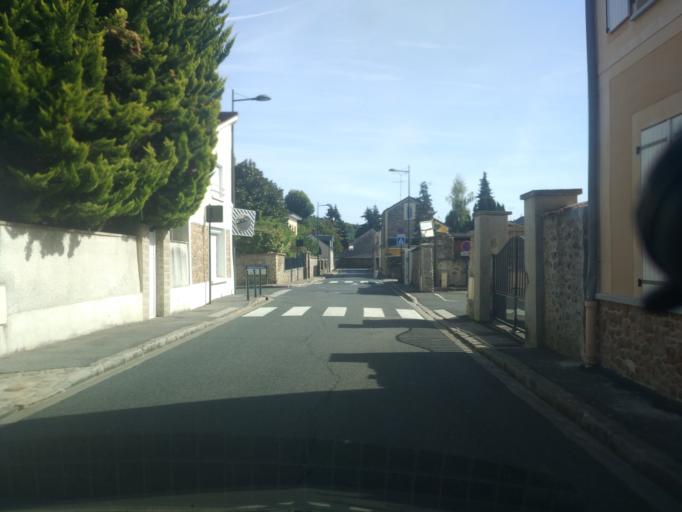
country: FR
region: Ile-de-France
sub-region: Departement de l'Essonne
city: Limours
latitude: 48.6469
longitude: 2.0765
